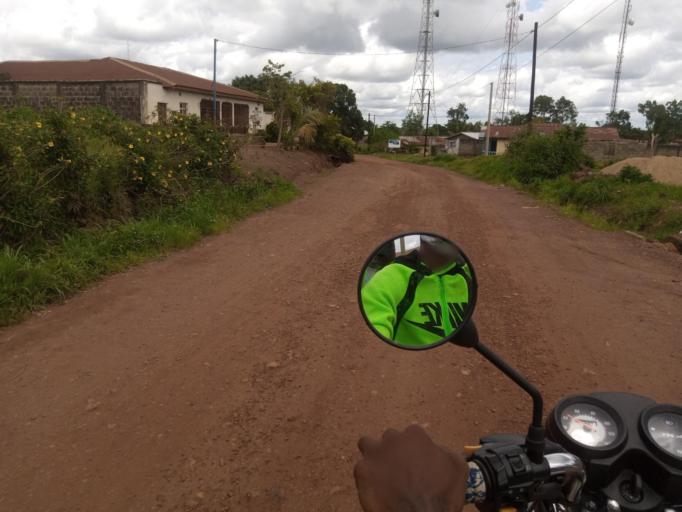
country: SL
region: Northern Province
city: Port Loko
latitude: 8.7631
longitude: -12.7808
